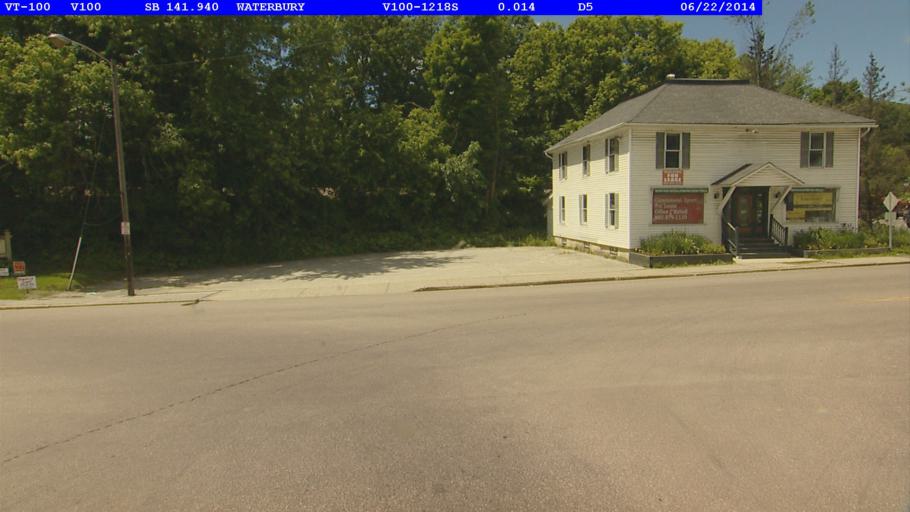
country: US
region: Vermont
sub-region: Washington County
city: Waterbury
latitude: 44.3414
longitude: -72.7594
